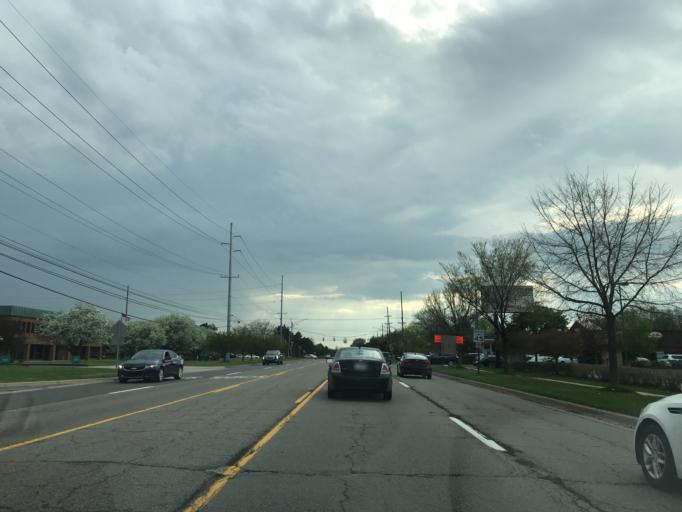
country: US
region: Michigan
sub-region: Oakland County
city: Farmington Hills
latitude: 42.4989
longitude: -83.3743
